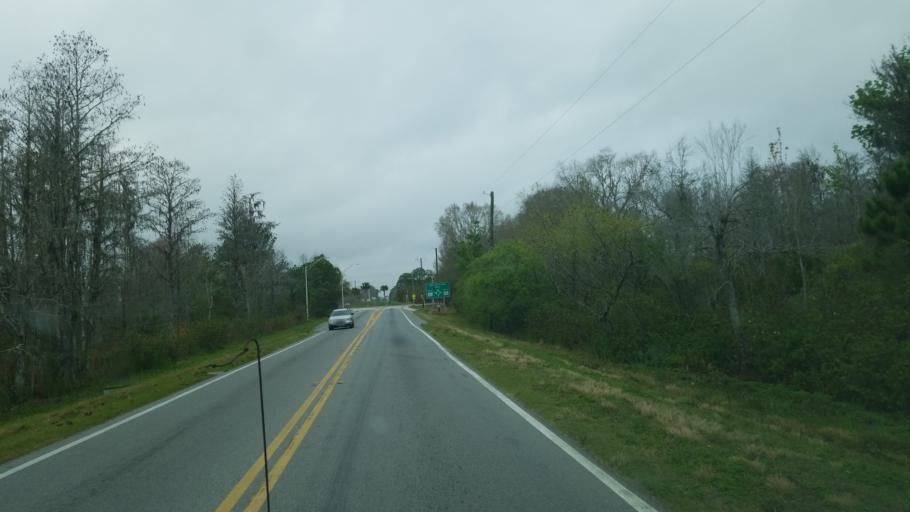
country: US
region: Florida
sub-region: Polk County
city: Polk City
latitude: 28.2585
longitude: -81.8223
